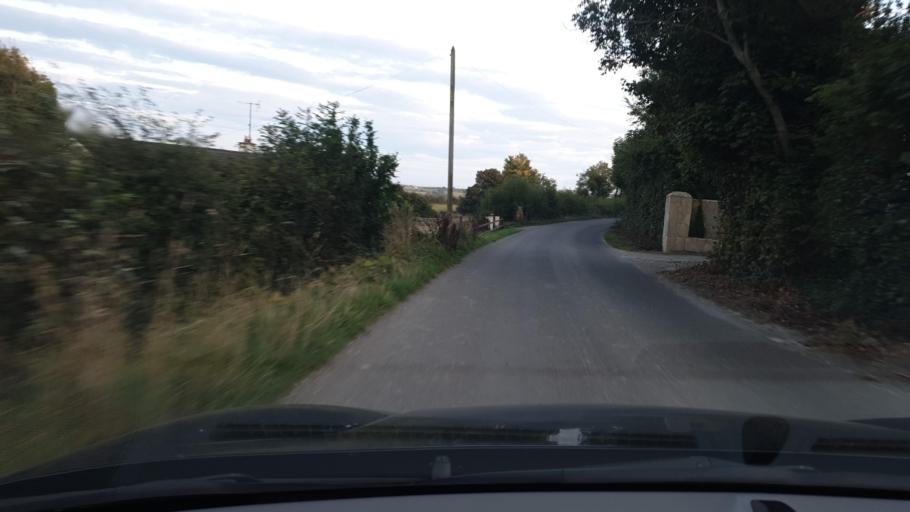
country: IE
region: Leinster
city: Balrothery
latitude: 53.5659
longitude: -6.2319
